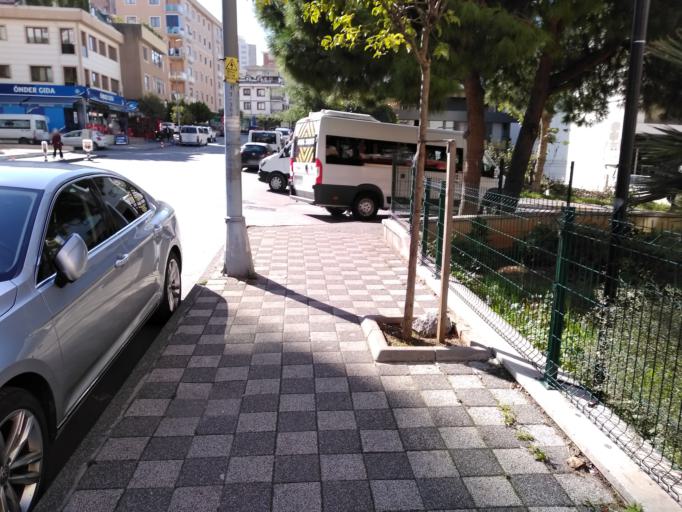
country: TR
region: Istanbul
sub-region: Atasehir
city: Atasehir
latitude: 40.9814
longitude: 29.1191
